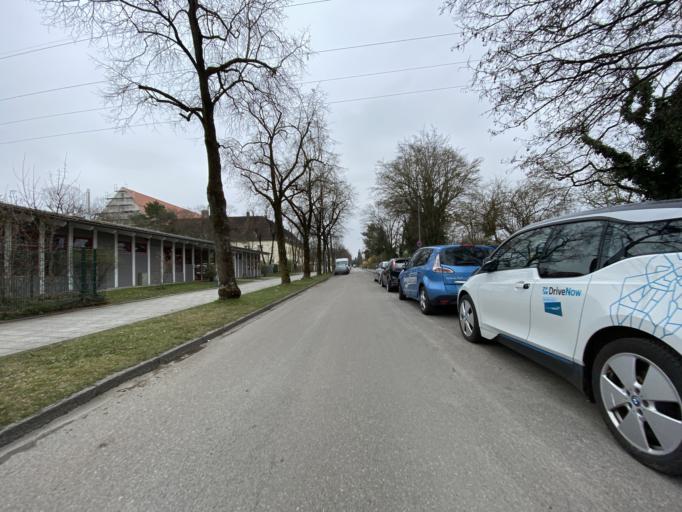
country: DE
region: Bavaria
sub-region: Upper Bavaria
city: Oberschleissheim
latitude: 48.1991
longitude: 11.5811
